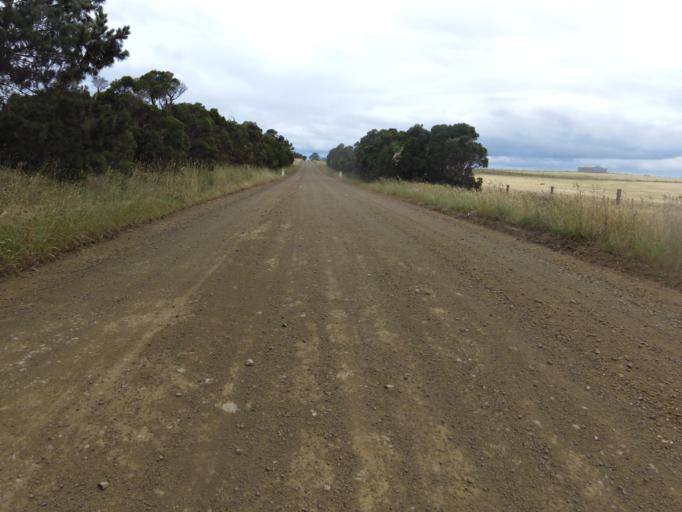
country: AU
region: Victoria
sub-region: Bass Coast
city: Cowes
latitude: -38.3888
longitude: 145.3426
